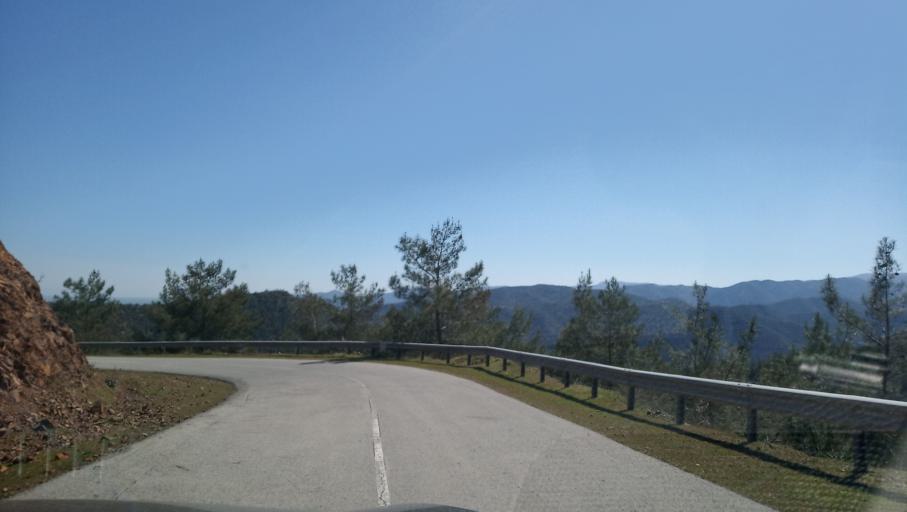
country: CY
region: Lefkosia
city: Lefka
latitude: 35.0799
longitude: 32.7740
